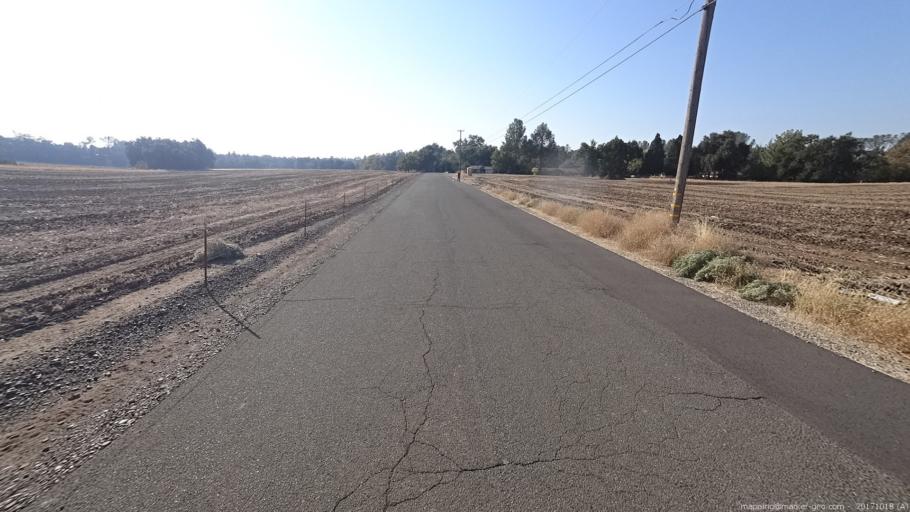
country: US
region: California
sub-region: Shasta County
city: Redding
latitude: 40.5600
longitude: -122.3699
